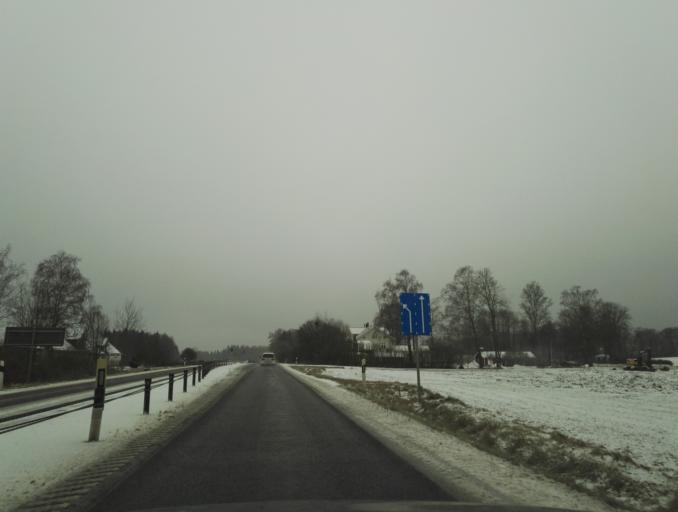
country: SE
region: Kronoberg
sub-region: Alvesta Kommun
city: Vislanda
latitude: 56.7309
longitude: 14.4803
